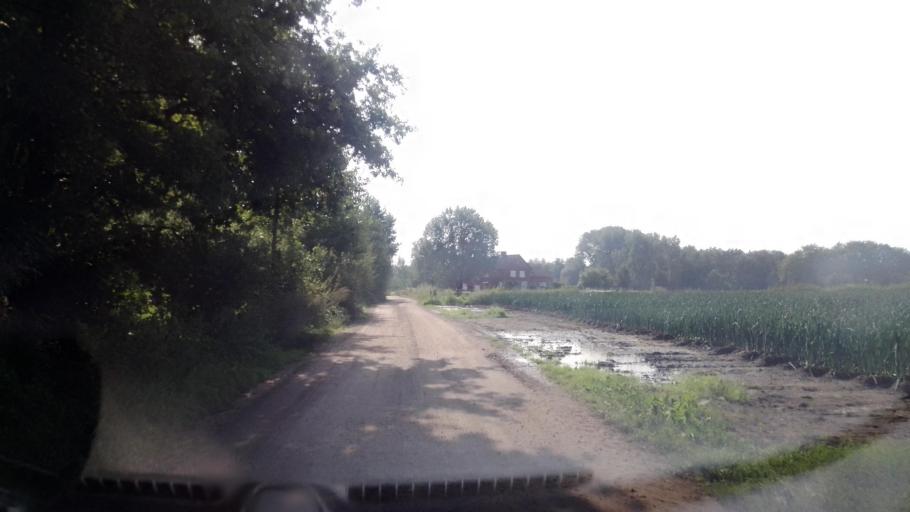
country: NL
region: Limburg
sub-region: Gemeente Peel en Maas
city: Maasbree
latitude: 51.3515
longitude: 6.0333
